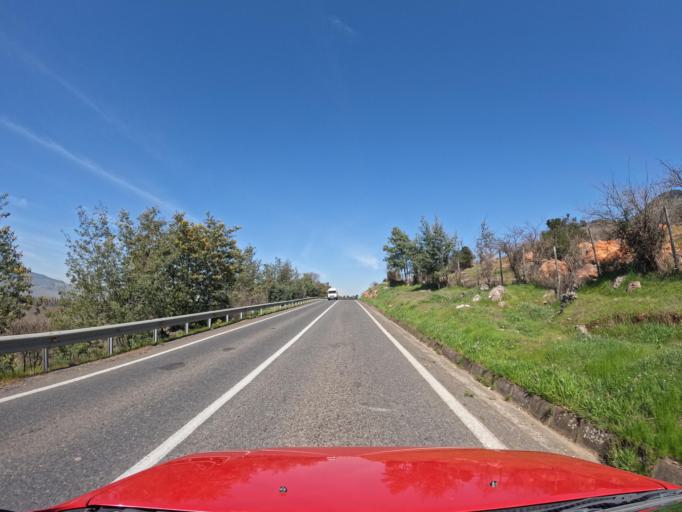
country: CL
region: Maule
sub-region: Provincia de Curico
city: Rauco
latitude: -35.0662
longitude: -71.6235
